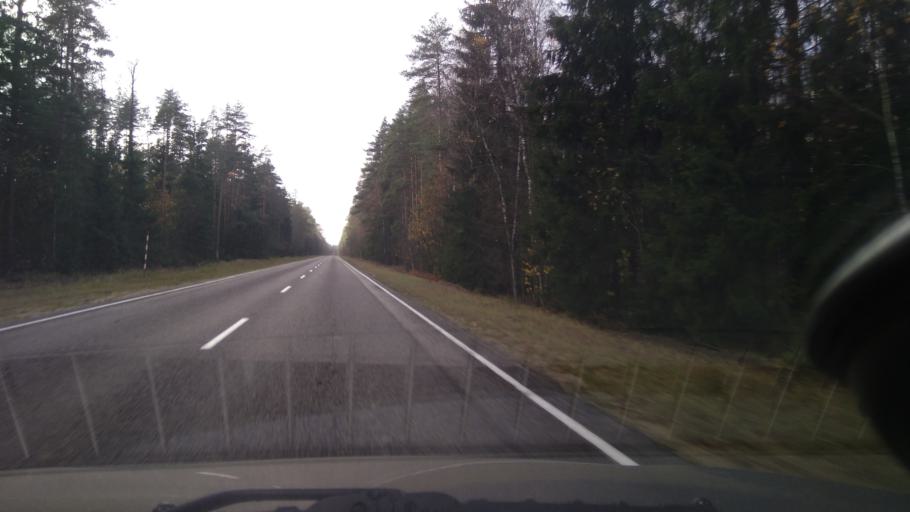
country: BY
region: Minsk
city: Urechcha
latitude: 53.2126
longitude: 27.8221
